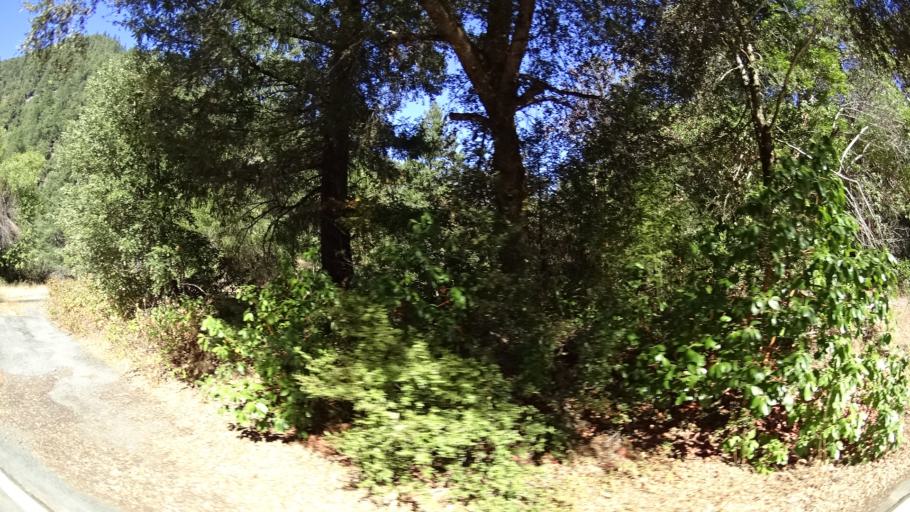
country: US
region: California
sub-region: Siskiyou County
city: Happy Camp
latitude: 41.3756
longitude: -123.4217
